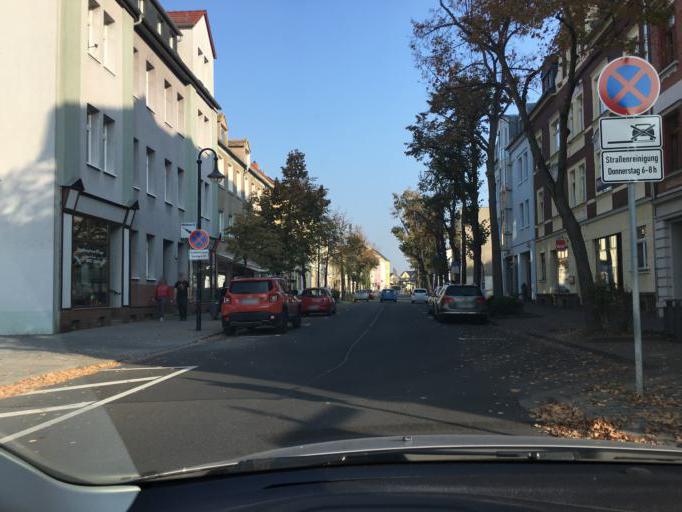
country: DE
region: Saxony
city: Wurzen
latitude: 51.3704
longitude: 12.7405
